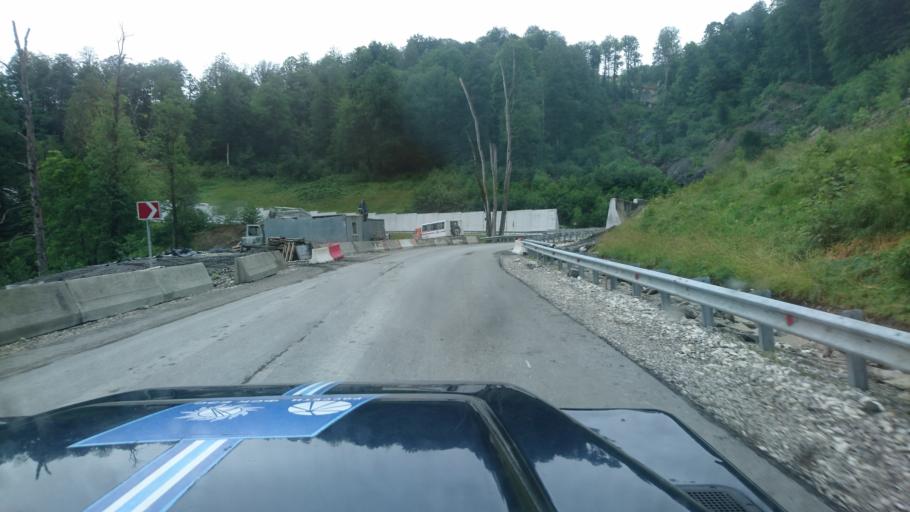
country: RU
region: Krasnodarskiy
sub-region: Sochi City
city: Krasnaya Polyana
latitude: 43.6600
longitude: 40.3098
